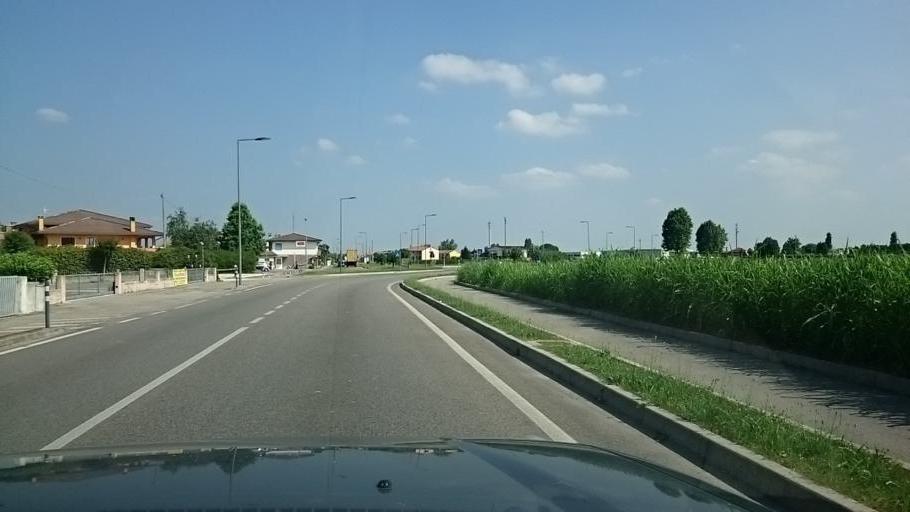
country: IT
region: Veneto
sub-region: Provincia di Padova
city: Abbazia Pisani
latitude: 45.6138
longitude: 11.8525
